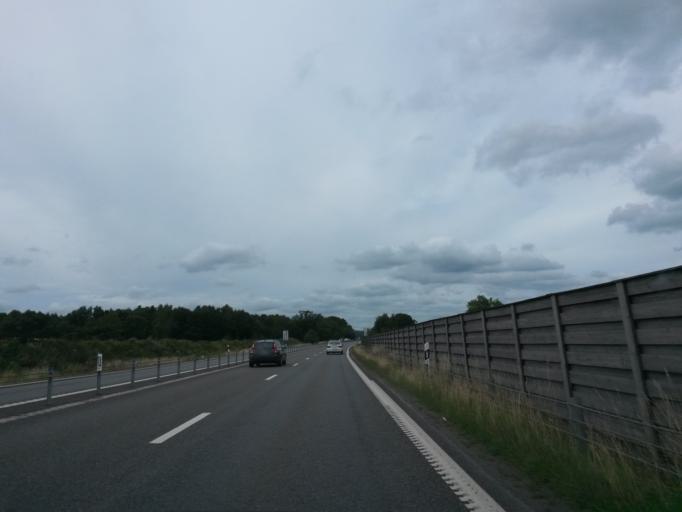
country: SE
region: Halland
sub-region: Varbergs Kommun
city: Varberg
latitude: 57.1505
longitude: 12.2691
